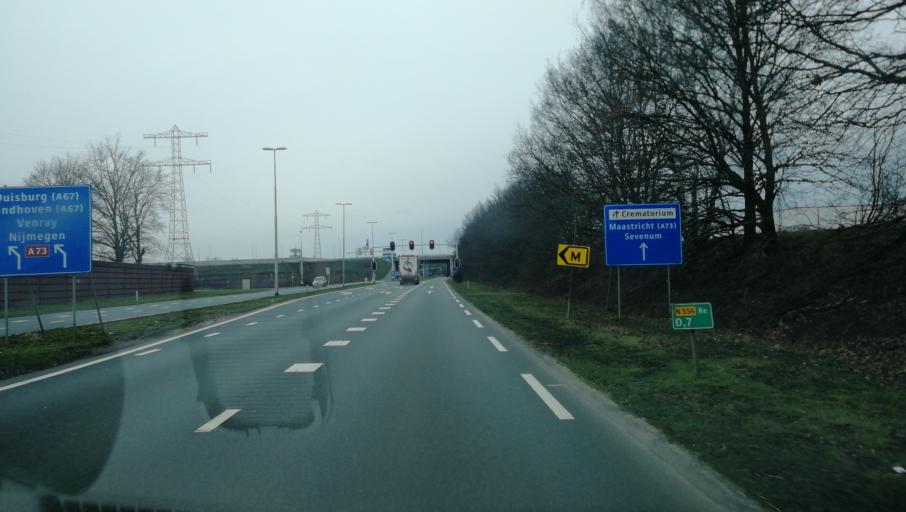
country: NL
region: Limburg
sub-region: Gemeente Venlo
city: Tegelen
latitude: 51.3840
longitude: 6.1290
